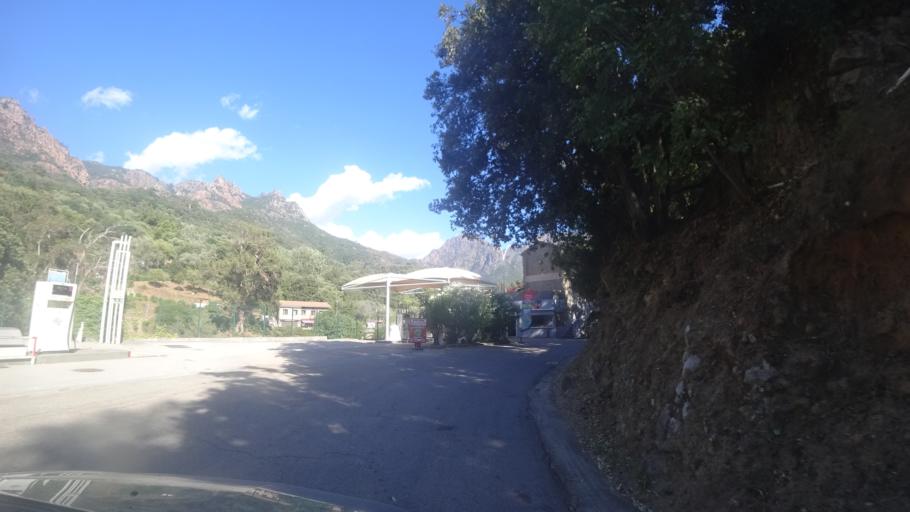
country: FR
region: Corsica
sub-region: Departement de la Corse-du-Sud
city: Cargese
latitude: 42.2624
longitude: 8.7087
